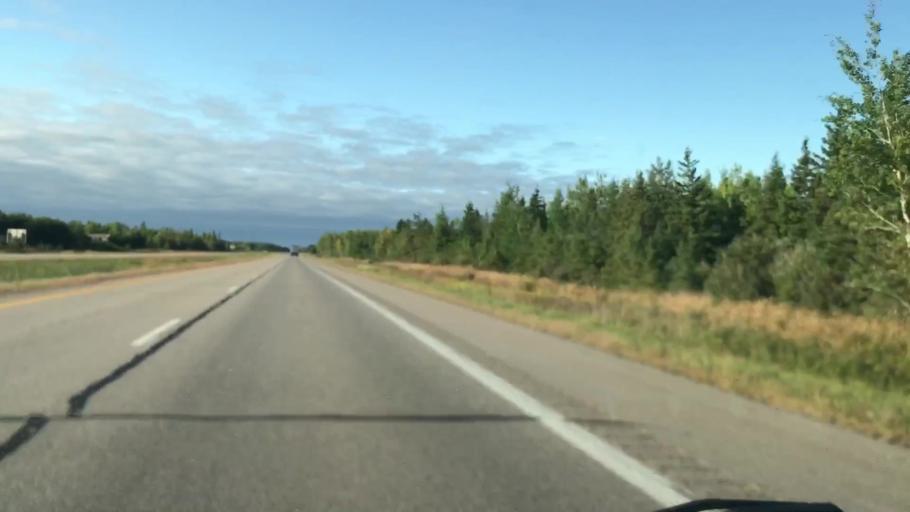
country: US
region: Michigan
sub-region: Chippewa County
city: Sault Ste. Marie
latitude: 46.4071
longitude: -84.4002
